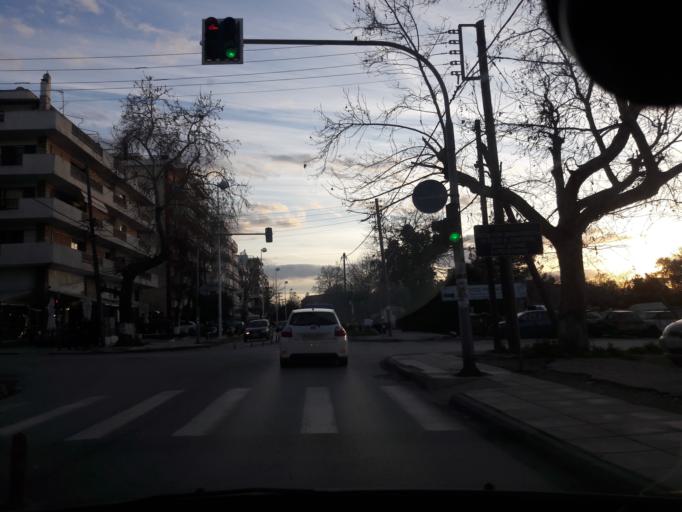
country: GR
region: Central Macedonia
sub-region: Nomos Thessalonikis
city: Kalamaria
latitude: 40.5879
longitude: 22.9432
